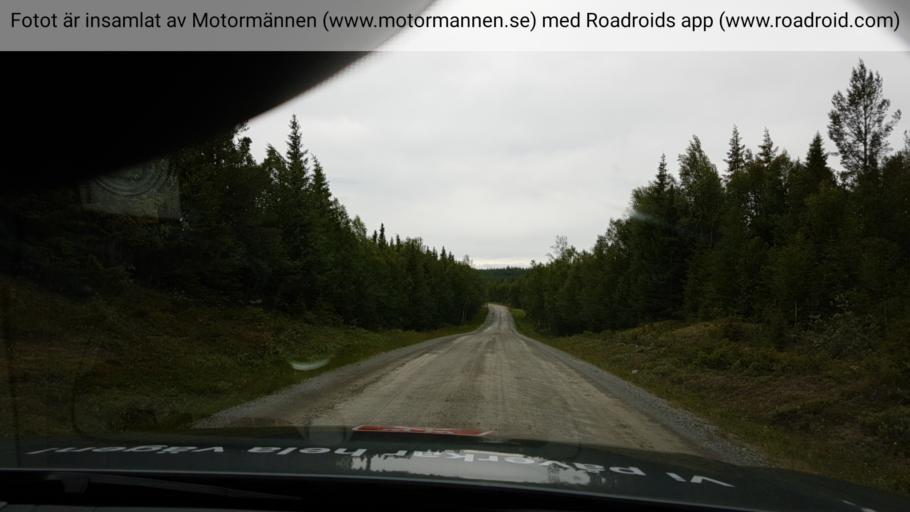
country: SE
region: Jaemtland
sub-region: Bergs Kommun
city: Hoverberg
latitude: 62.8460
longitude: 13.8458
